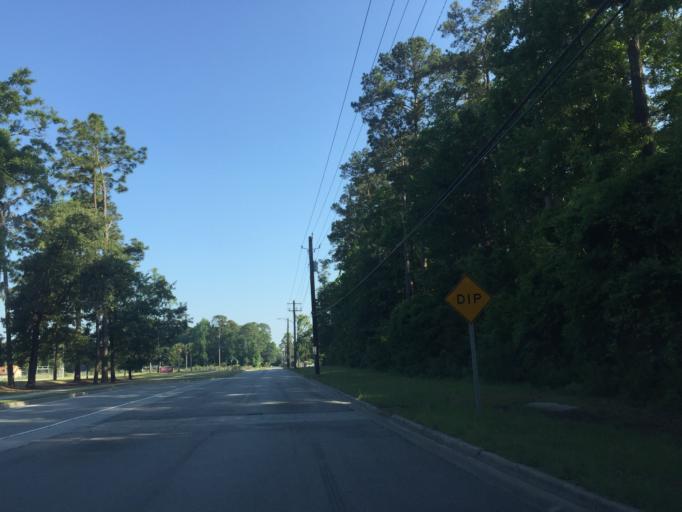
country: US
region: Georgia
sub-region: Chatham County
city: Isle of Hope
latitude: 31.9963
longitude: -81.0778
